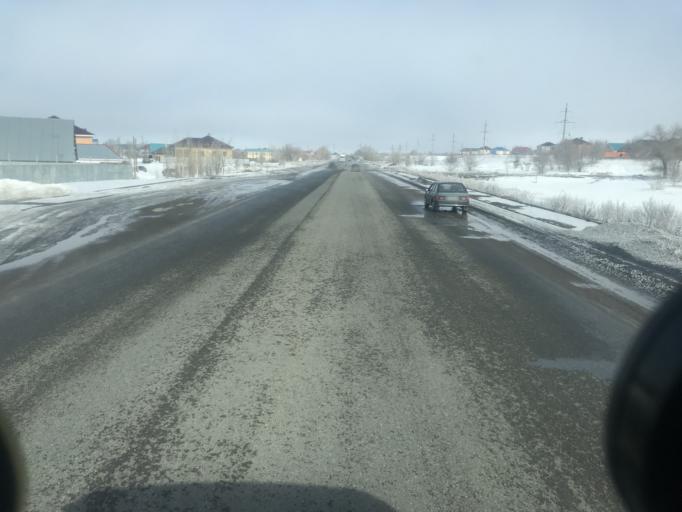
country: KZ
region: Aqtoebe
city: Aqtobe
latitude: 50.2814
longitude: 57.2821
